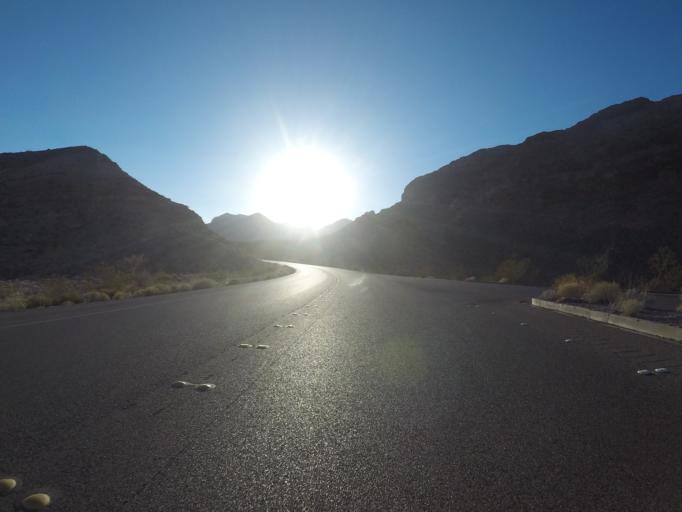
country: US
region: Nevada
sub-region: Clark County
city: Moapa Valley
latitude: 36.3616
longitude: -114.4813
